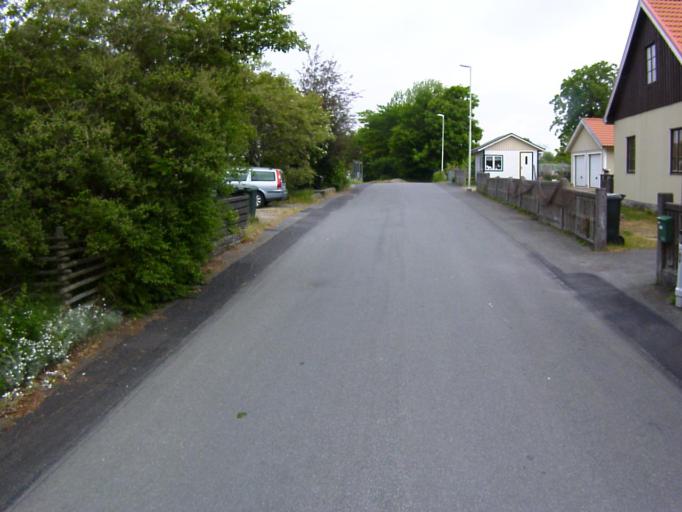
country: SE
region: Skane
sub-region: Kristianstads Kommun
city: Ahus
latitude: 55.9187
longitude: 14.2915
